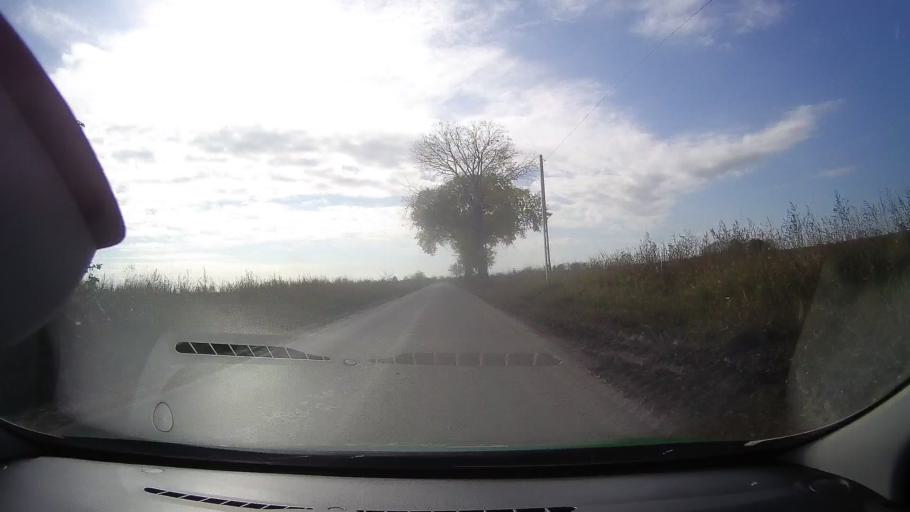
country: RO
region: Tulcea
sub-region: Comuna Valea Nucarilor
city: Agighiol
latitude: 44.9853
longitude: 28.8842
